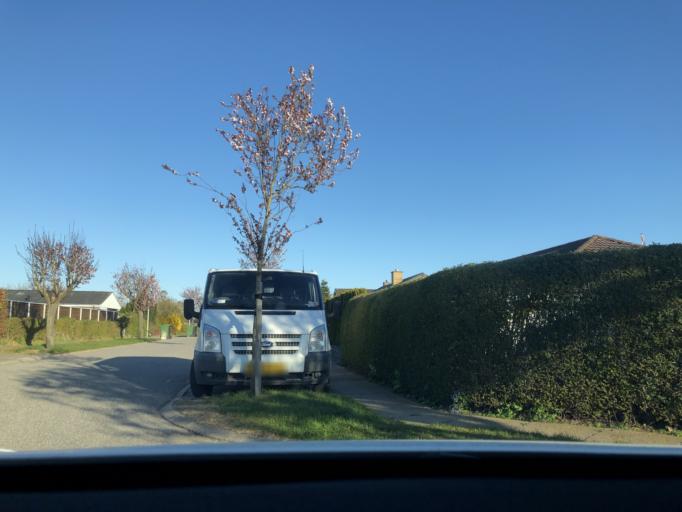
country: DK
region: Zealand
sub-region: Greve Kommune
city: Greve
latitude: 55.5820
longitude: 12.2801
